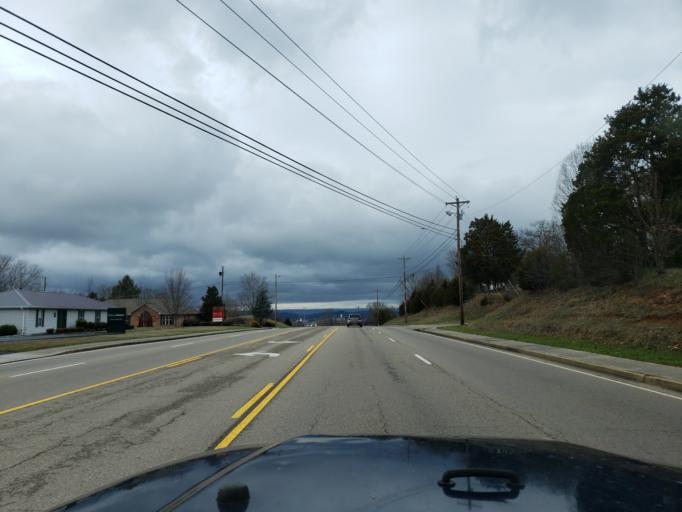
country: US
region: Tennessee
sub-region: Jefferson County
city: Jefferson City
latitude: 36.1028
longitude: -83.4831
